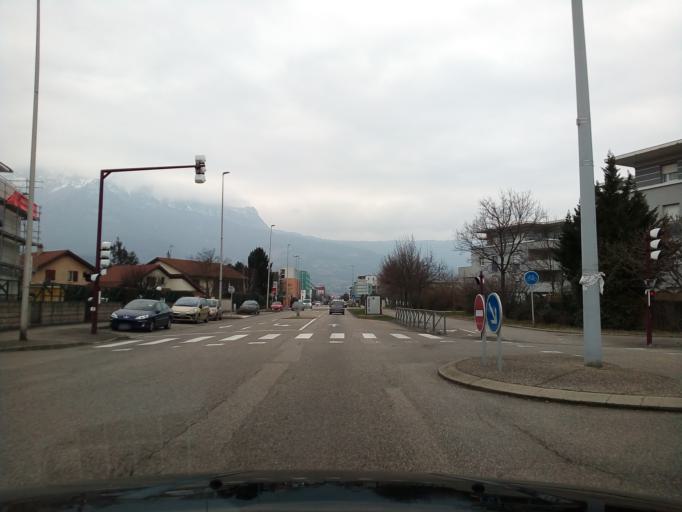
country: FR
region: Rhone-Alpes
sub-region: Departement de l'Isere
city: Echirolles
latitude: 45.1468
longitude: 5.7281
